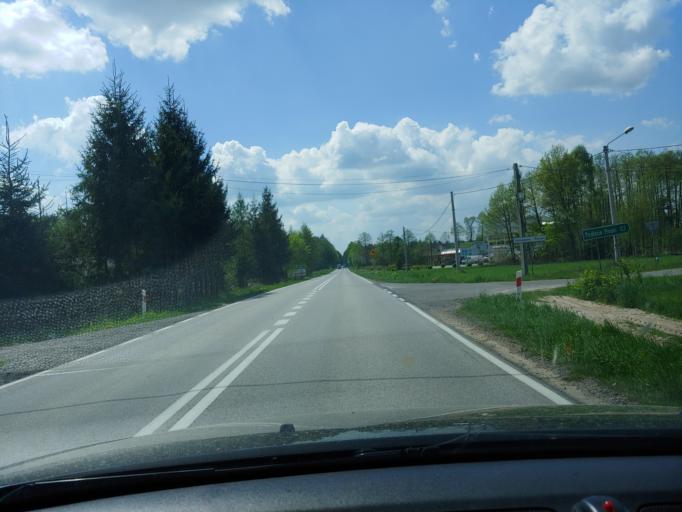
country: PL
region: Lesser Poland Voivodeship
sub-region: Powiat dabrowski
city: Radgoszcz
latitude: 50.1432
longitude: 21.1783
